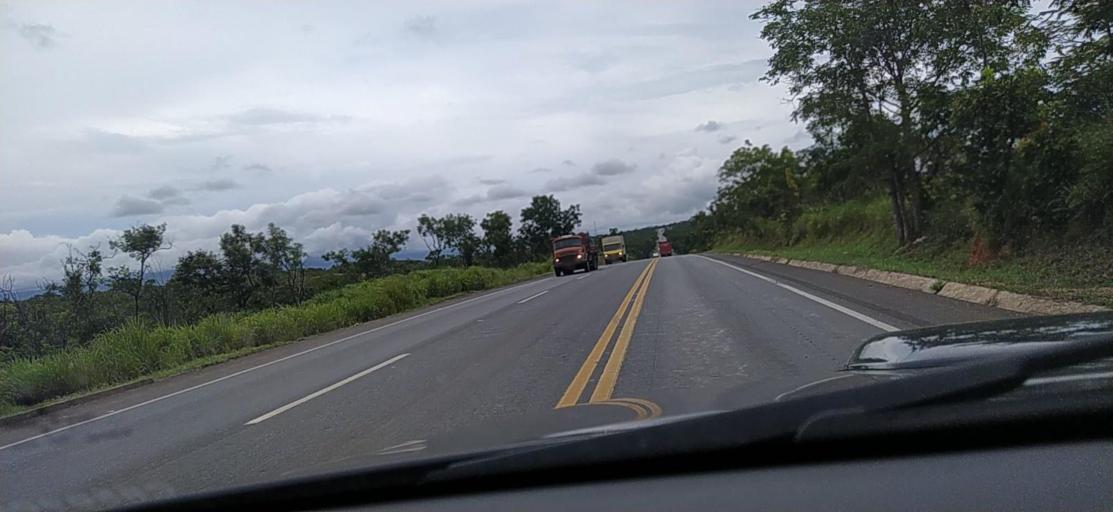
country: BR
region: Minas Gerais
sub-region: Corinto
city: Corinto
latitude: -18.3125
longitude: -44.4198
